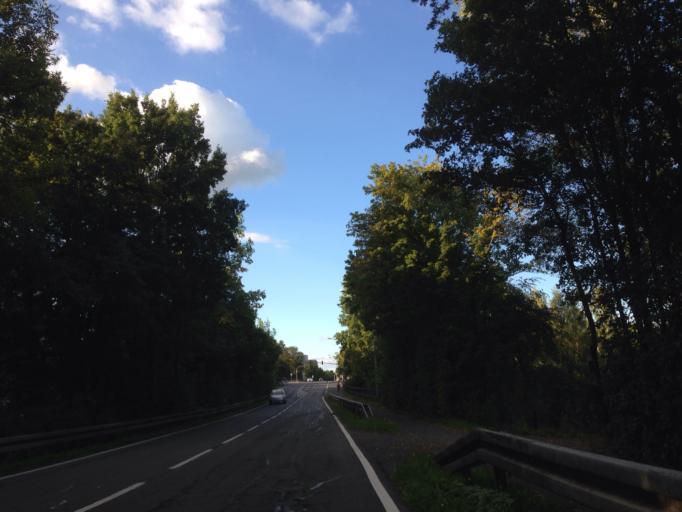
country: DE
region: Hesse
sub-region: Regierungsbezirk Giessen
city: Giessen
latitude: 50.5634
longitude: 8.6786
